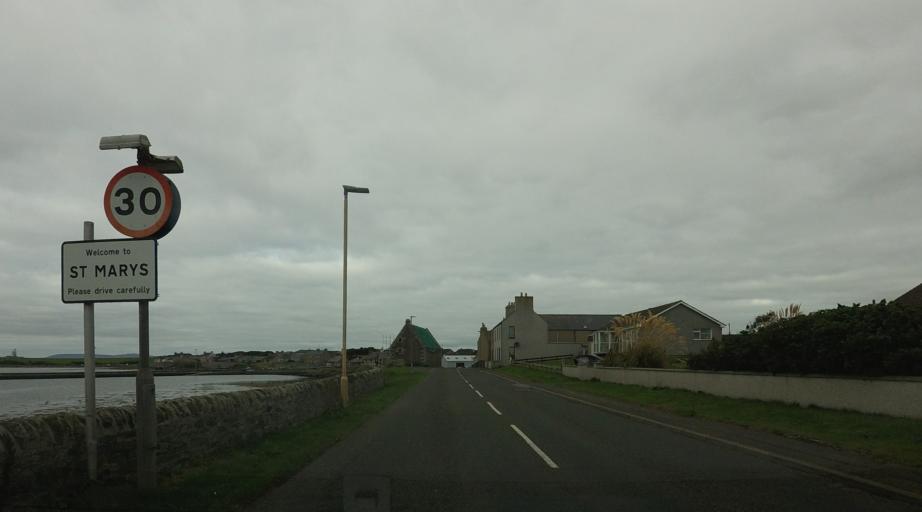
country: GB
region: Scotland
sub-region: Orkney Islands
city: Kirkwall
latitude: 58.8958
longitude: -2.9074
